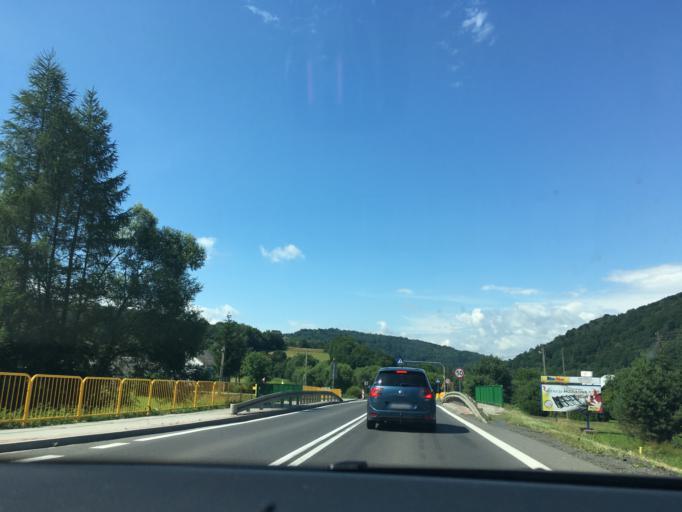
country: PL
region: Subcarpathian Voivodeship
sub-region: Powiat krosnienski
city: Dukla
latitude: 49.5116
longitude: 21.6954
